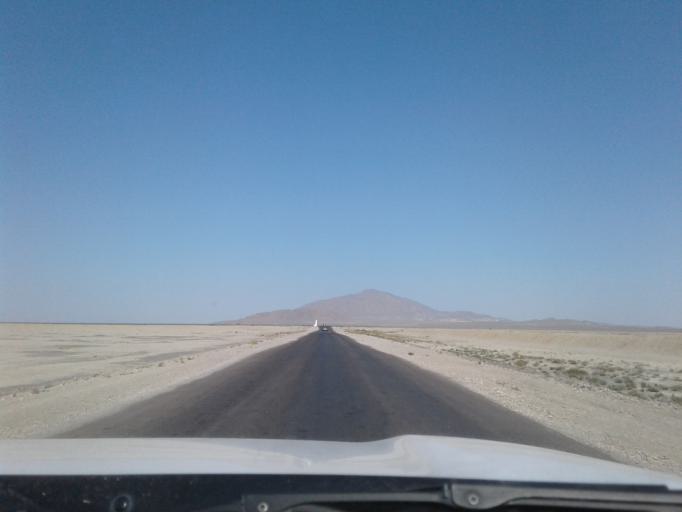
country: TM
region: Balkan
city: Gumdag
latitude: 39.2385
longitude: 54.7036
